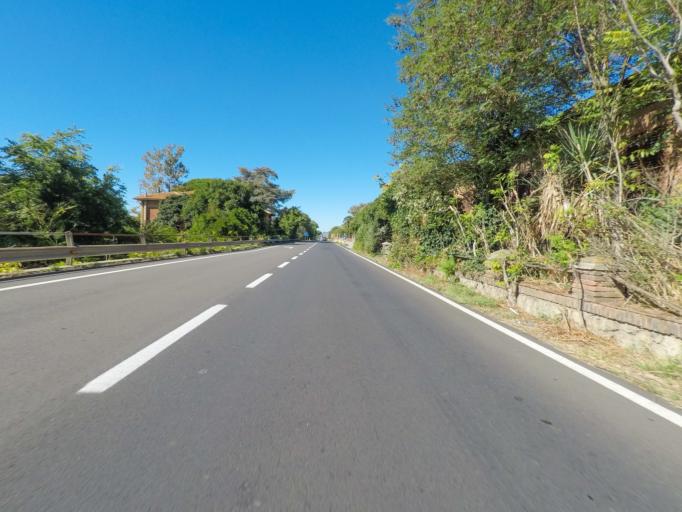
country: IT
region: Tuscany
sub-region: Provincia di Grosseto
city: Orbetello Scalo
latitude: 42.4516
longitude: 11.2541
